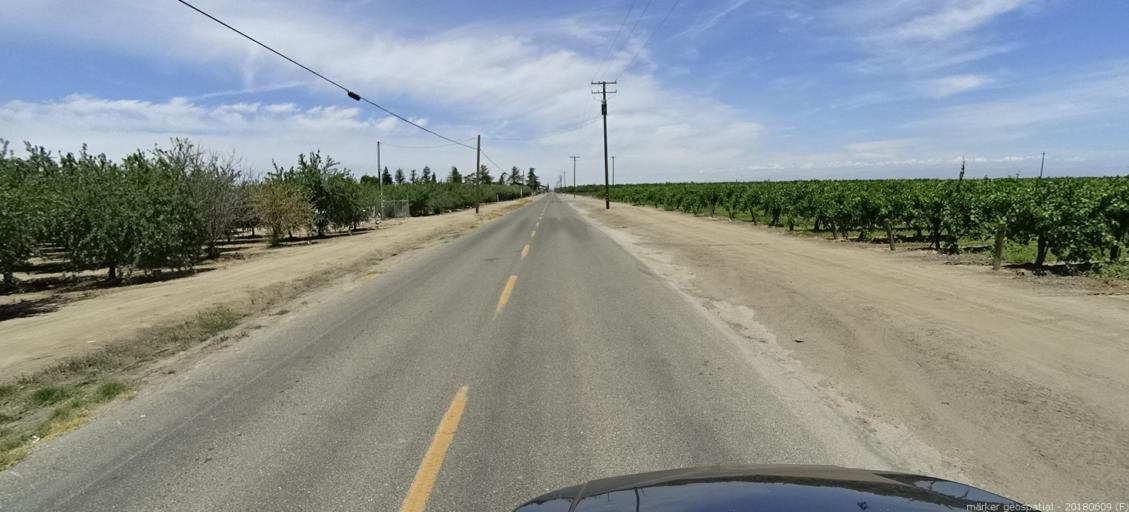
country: US
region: California
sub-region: Madera County
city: Parkwood
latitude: 36.8754
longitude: -120.0922
